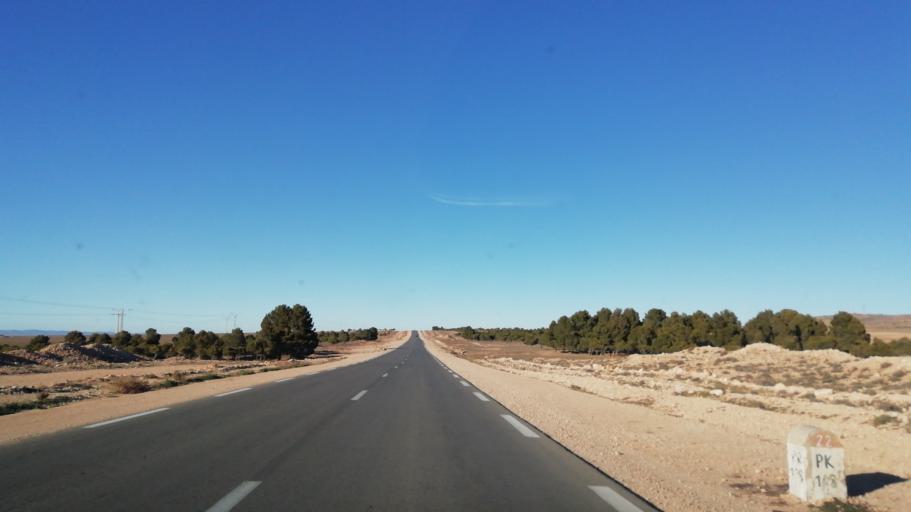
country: DZ
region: Tlemcen
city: Sebdou
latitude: 34.2509
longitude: -1.2574
